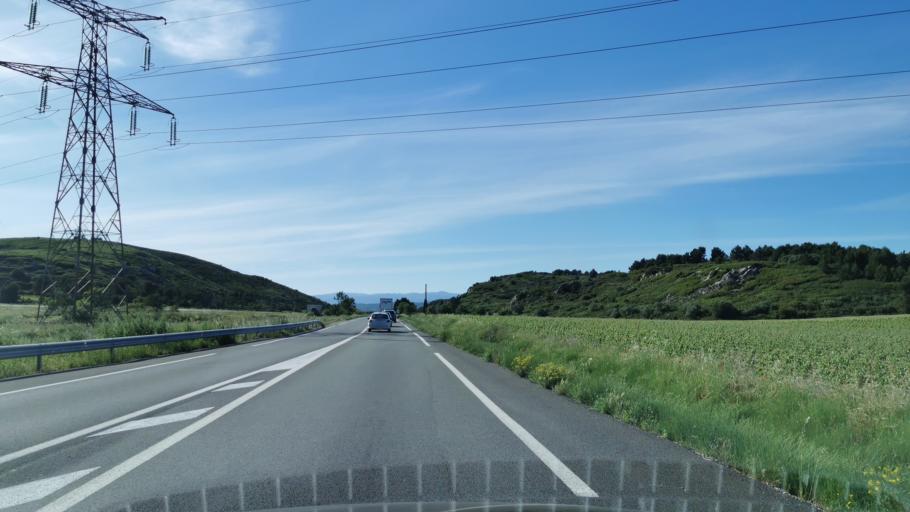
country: FR
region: Languedoc-Roussillon
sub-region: Departement de l'Aude
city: Nevian
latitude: 43.1991
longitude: 2.8971
